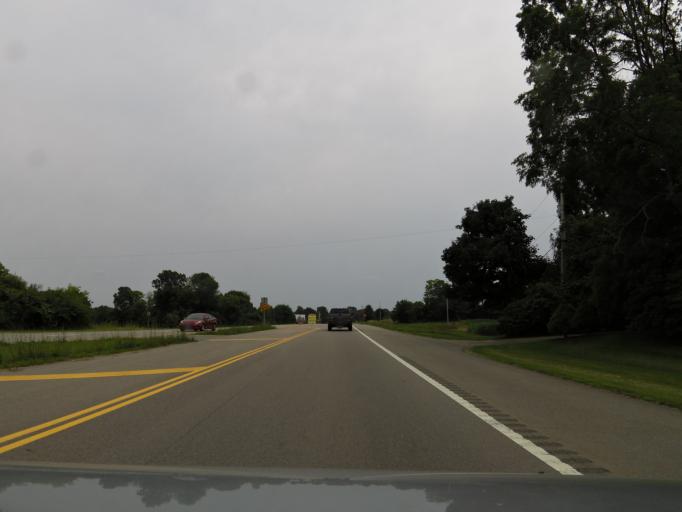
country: US
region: Ohio
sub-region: Warren County
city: Waynesville
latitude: 39.4996
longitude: -83.9969
